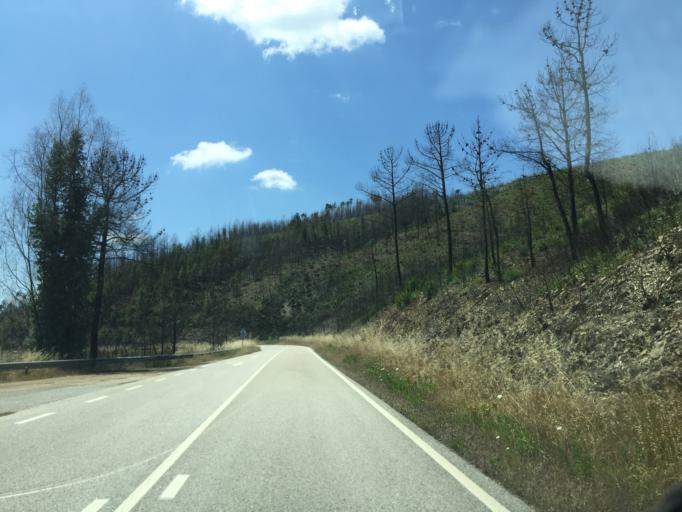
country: PT
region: Coimbra
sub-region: Pampilhosa da Serra
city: Pampilhosa da Serra
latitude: 40.0023
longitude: -8.0000
